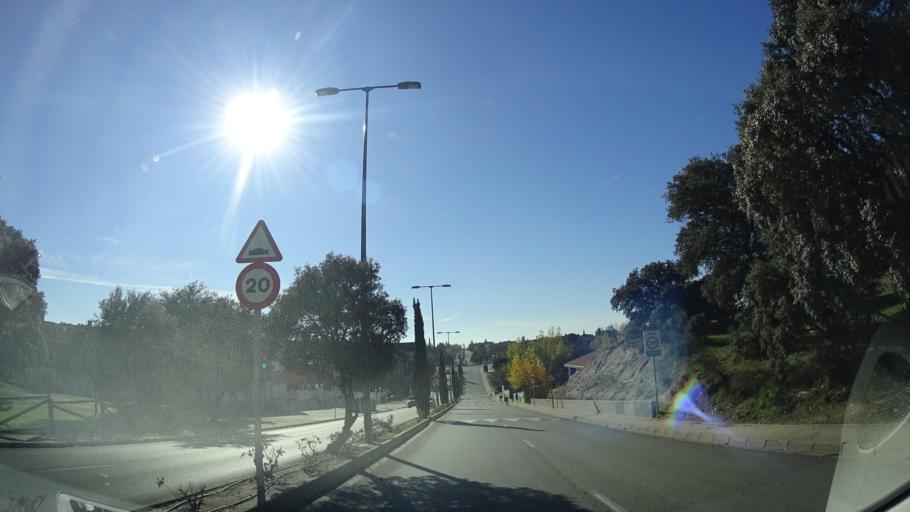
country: ES
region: Madrid
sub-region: Provincia de Madrid
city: Las Matas
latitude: 40.5274
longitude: -3.9155
